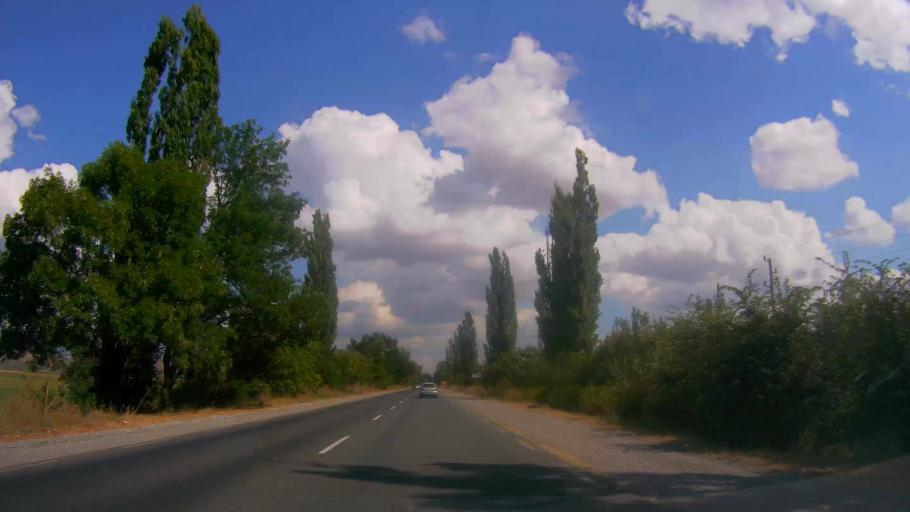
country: BG
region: Sliven
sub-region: Obshtina Sliven
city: Sliven
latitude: 42.6375
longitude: 26.2594
